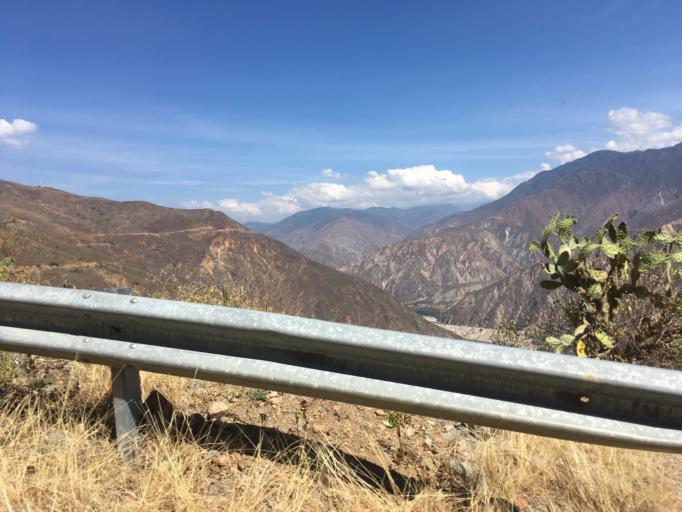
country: CO
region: Santander
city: Aratoca
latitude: 6.7713
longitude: -72.9909
